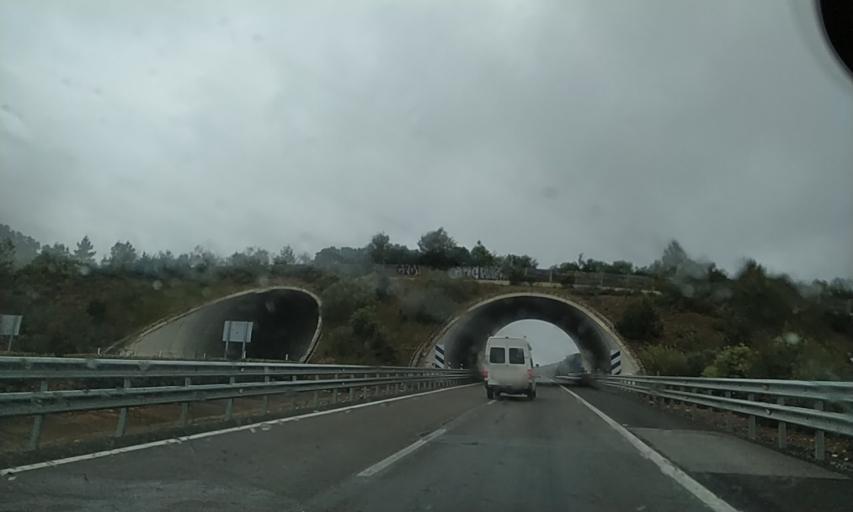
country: ES
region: Extremadura
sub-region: Provincia de Caceres
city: Casas de Millan
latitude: 39.8294
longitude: -6.3614
